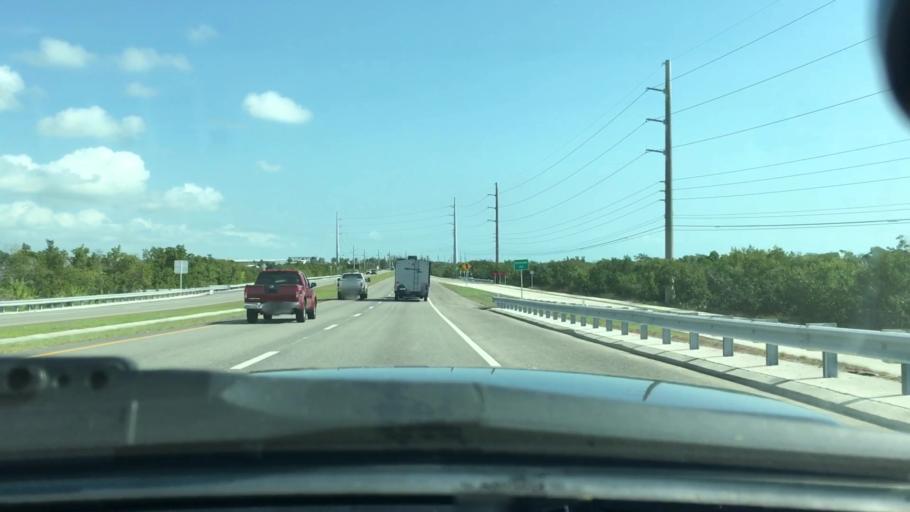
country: US
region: Florida
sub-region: Monroe County
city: Big Coppitt Key
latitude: 24.5883
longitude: -81.6887
